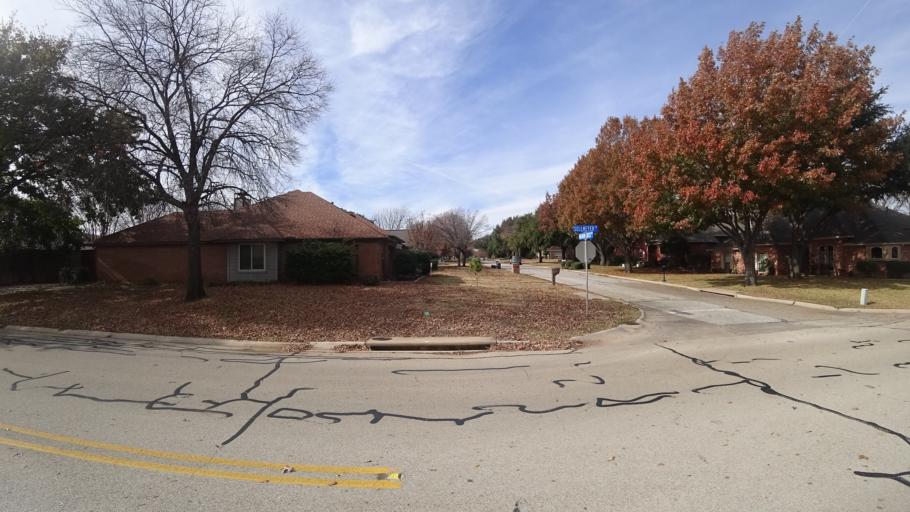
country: US
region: Texas
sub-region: Denton County
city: Highland Village
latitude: 33.0730
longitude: -97.0460
